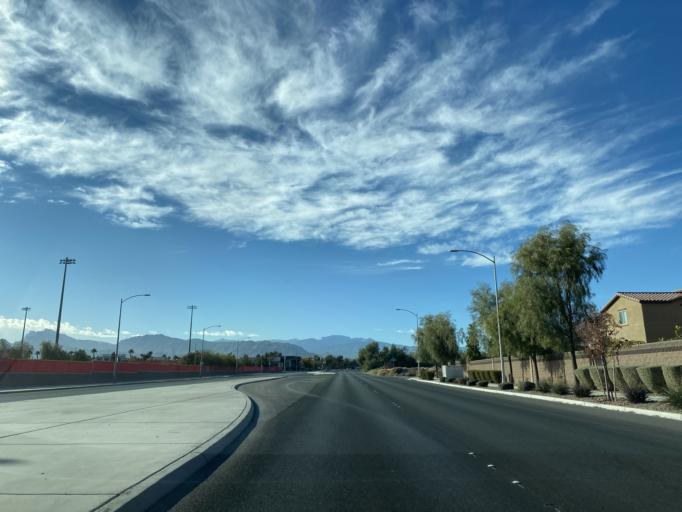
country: US
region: Nevada
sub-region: Clark County
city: North Las Vegas
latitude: 36.3052
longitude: -115.2568
